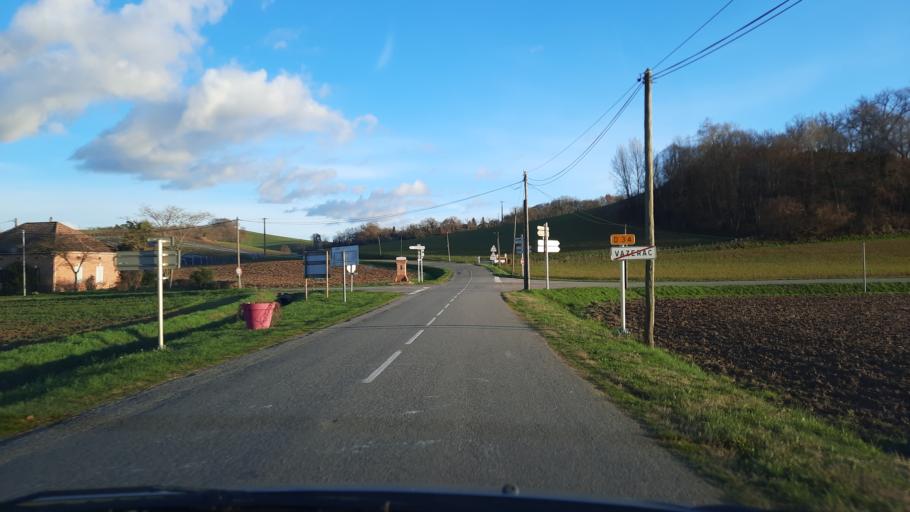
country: FR
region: Midi-Pyrenees
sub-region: Departement du Tarn-et-Garonne
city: Lafrancaise
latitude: 44.1880
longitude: 1.2867
